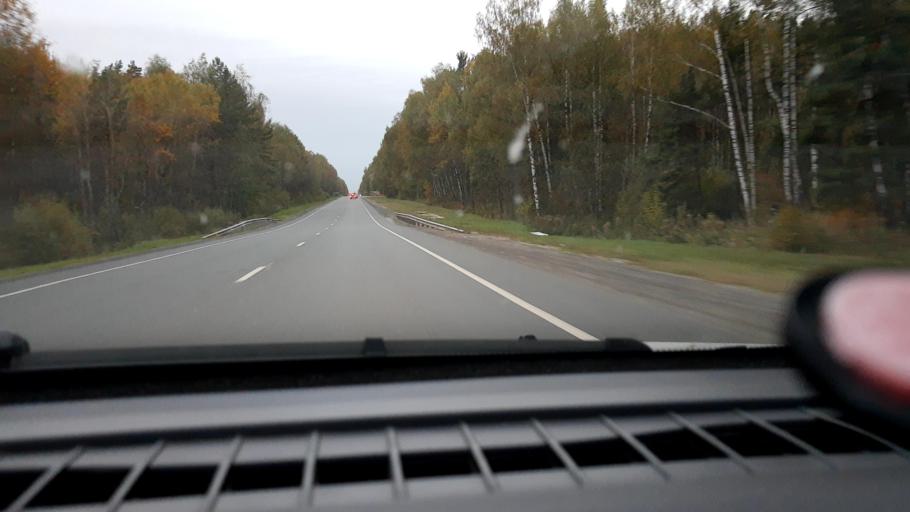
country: RU
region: Vladimir
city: Orgtrud
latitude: 56.2099
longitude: 40.6355
